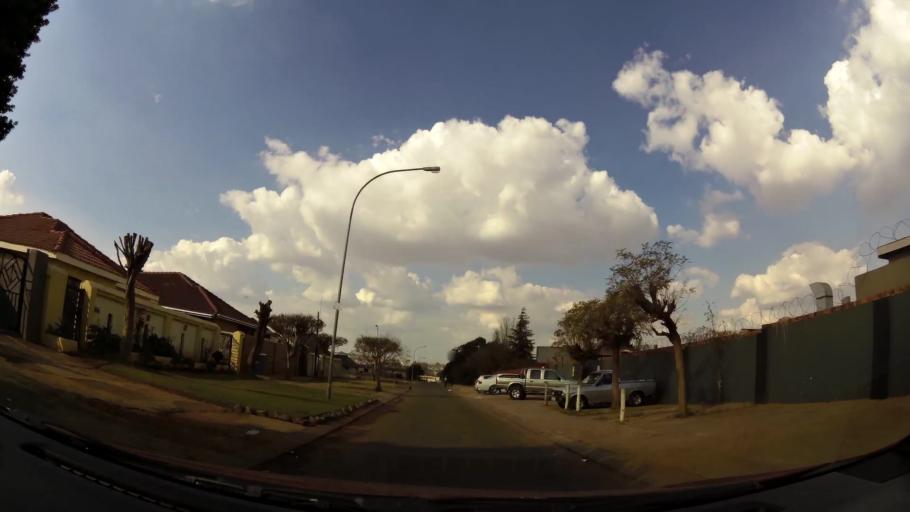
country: ZA
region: Gauteng
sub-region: City of Johannesburg Metropolitan Municipality
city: Roodepoort
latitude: -26.2136
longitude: 27.8660
